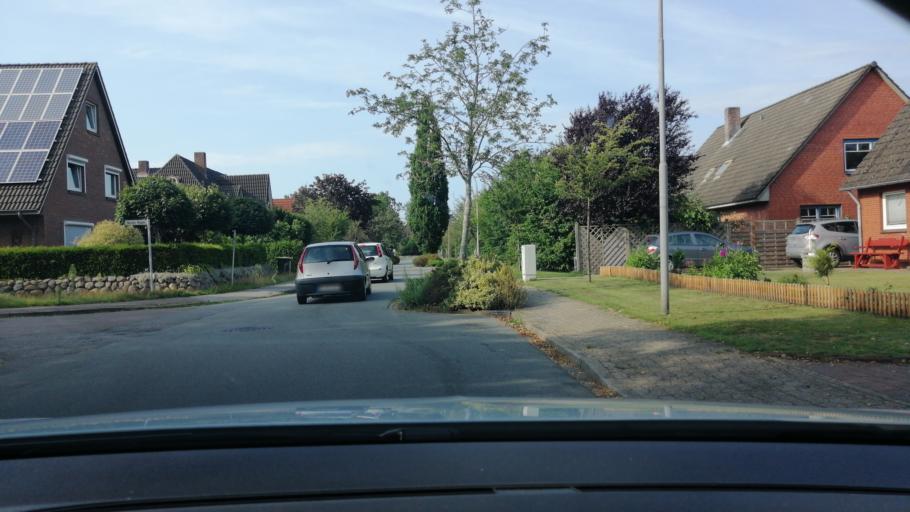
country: DE
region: Schleswig-Holstein
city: Leck
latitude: 54.7702
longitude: 8.9624
